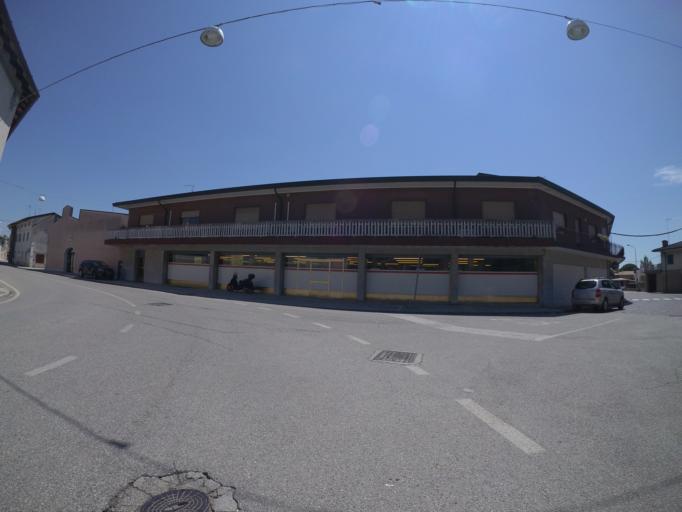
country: IT
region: Friuli Venezia Giulia
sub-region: Provincia di Udine
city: Talmassons
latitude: 45.9210
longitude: 13.1400
